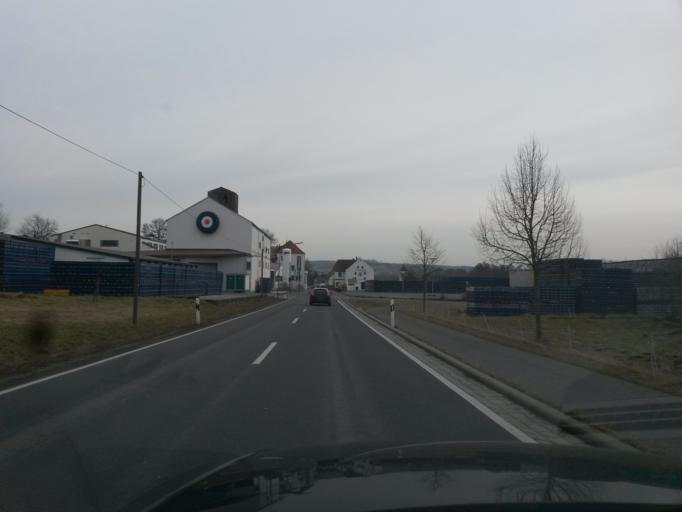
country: DE
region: Bavaria
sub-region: Regierungsbezirk Unterfranken
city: Ostheim vor der Rhon
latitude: 50.4607
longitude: 10.2182
